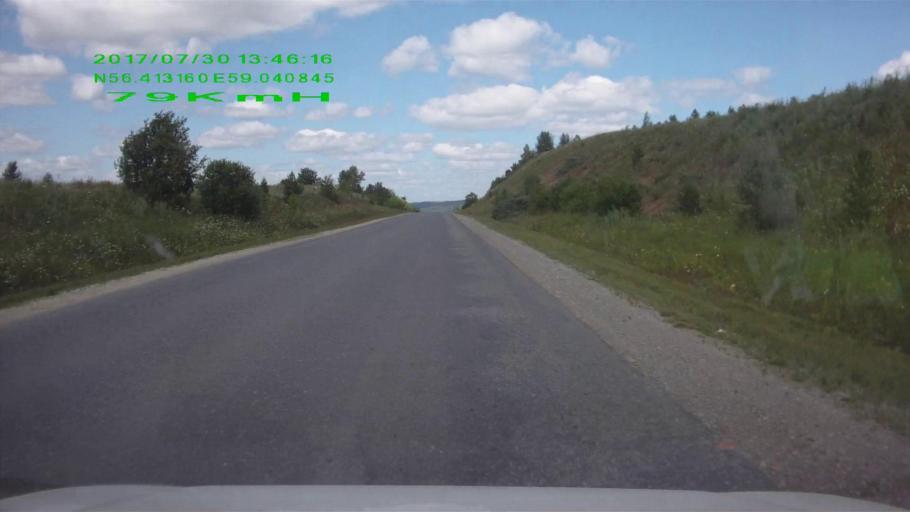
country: RU
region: Sverdlovsk
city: Mikhaylovsk
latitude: 56.4134
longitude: 59.0409
